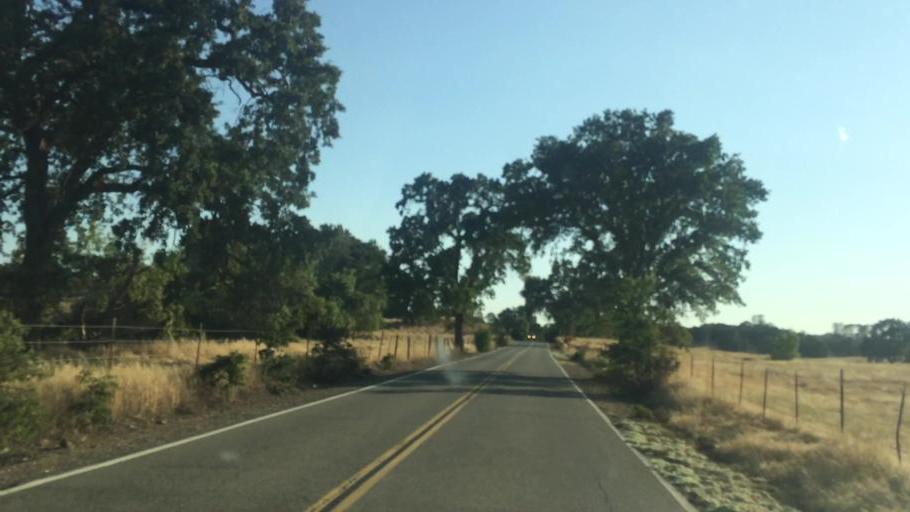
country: US
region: California
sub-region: Amador County
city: Plymouth
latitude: 38.4825
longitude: -120.9286
